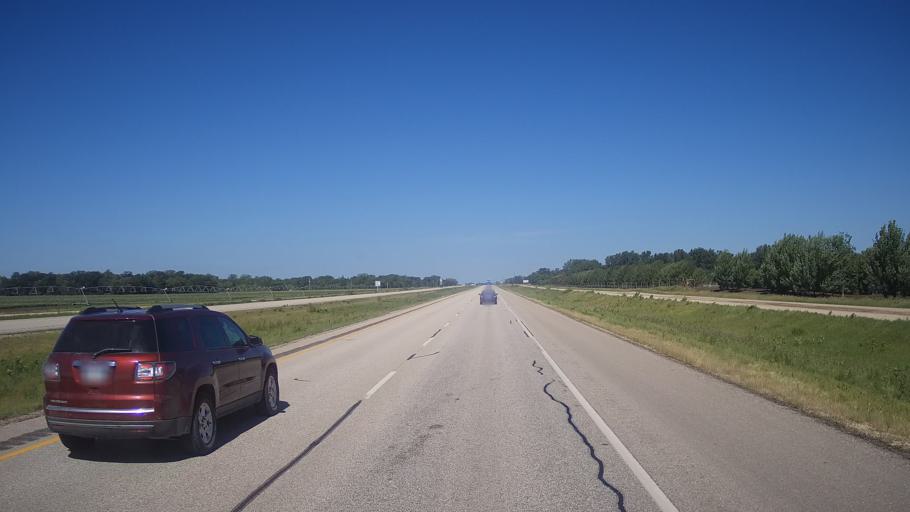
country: CA
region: Manitoba
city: Portage la Prairie
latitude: 49.9474
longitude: -98.3036
